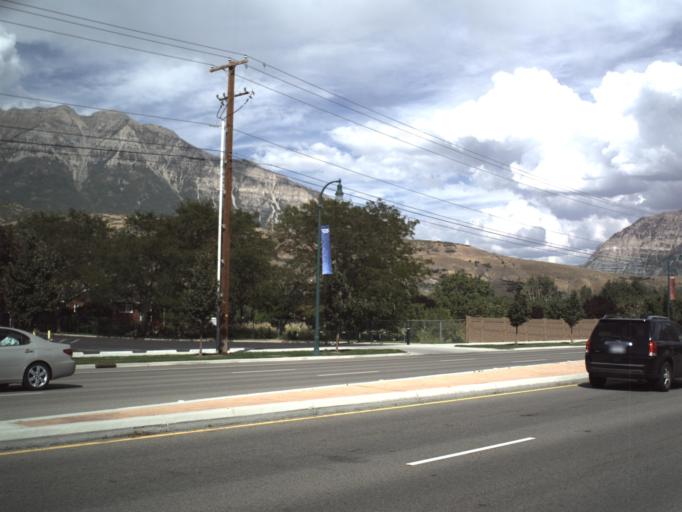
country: US
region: Utah
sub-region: Utah County
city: Orem
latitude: 40.3119
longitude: -111.6856
